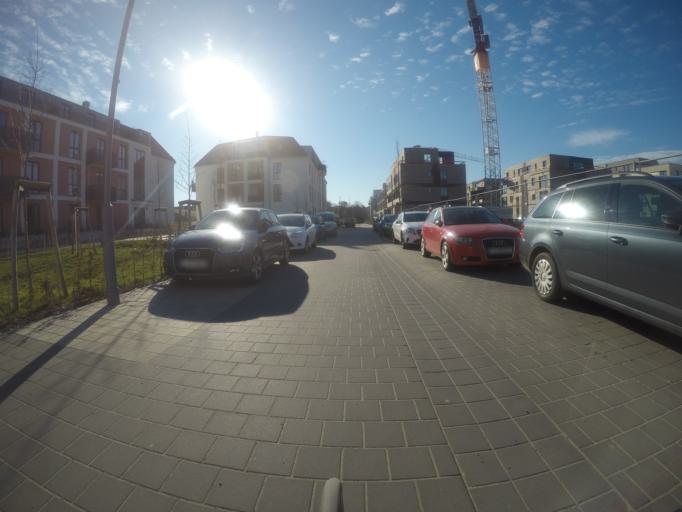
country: DE
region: Berlin
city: Grunau
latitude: 52.4247
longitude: 13.5778
